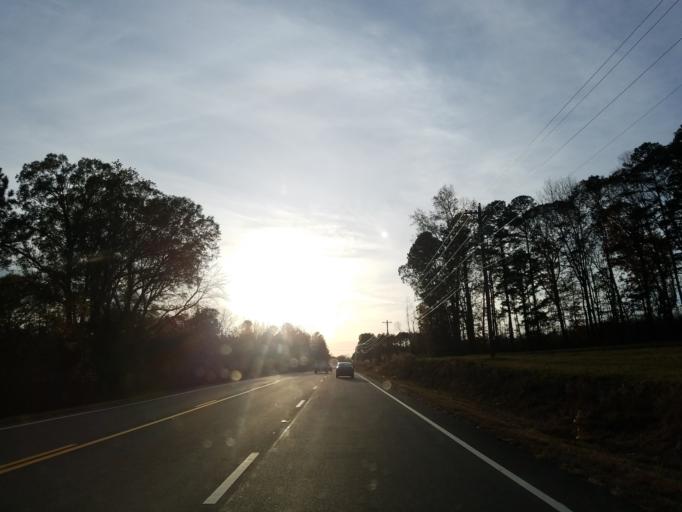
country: US
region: Georgia
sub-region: Carroll County
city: Temple
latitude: 33.7274
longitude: -85.0740
